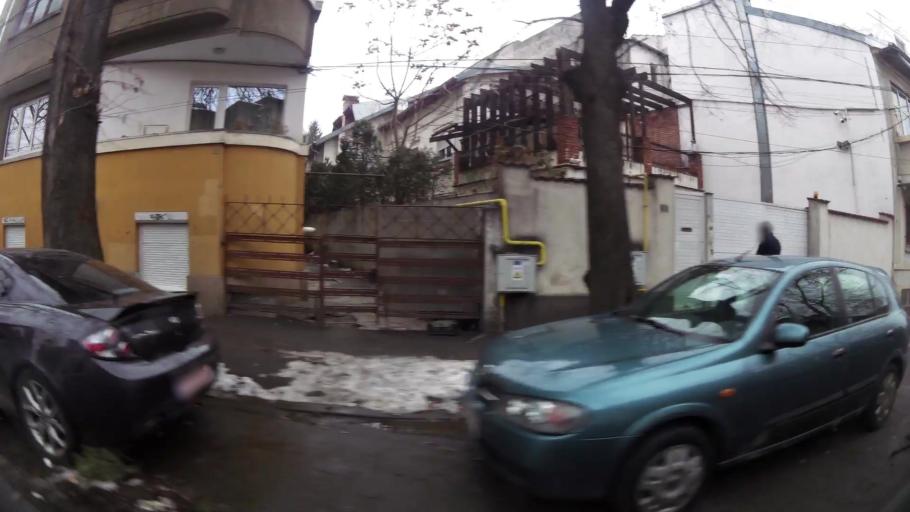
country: RO
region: Bucuresti
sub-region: Municipiul Bucuresti
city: Bucharest
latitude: 44.4513
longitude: 26.1081
